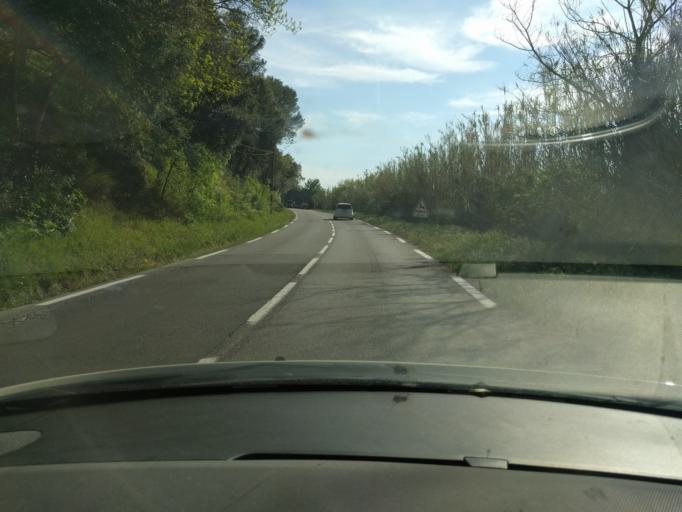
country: FR
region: Provence-Alpes-Cote d'Azur
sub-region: Departement du Var
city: Pierrefeu-du-Var
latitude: 43.2071
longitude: 6.1370
